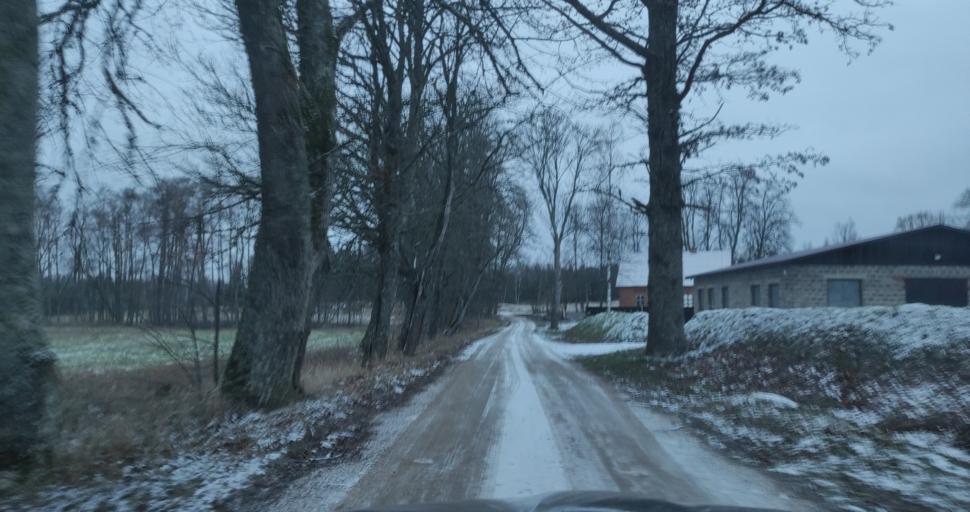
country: LV
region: Kuldigas Rajons
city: Kuldiga
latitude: 56.9769
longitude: 22.0539
